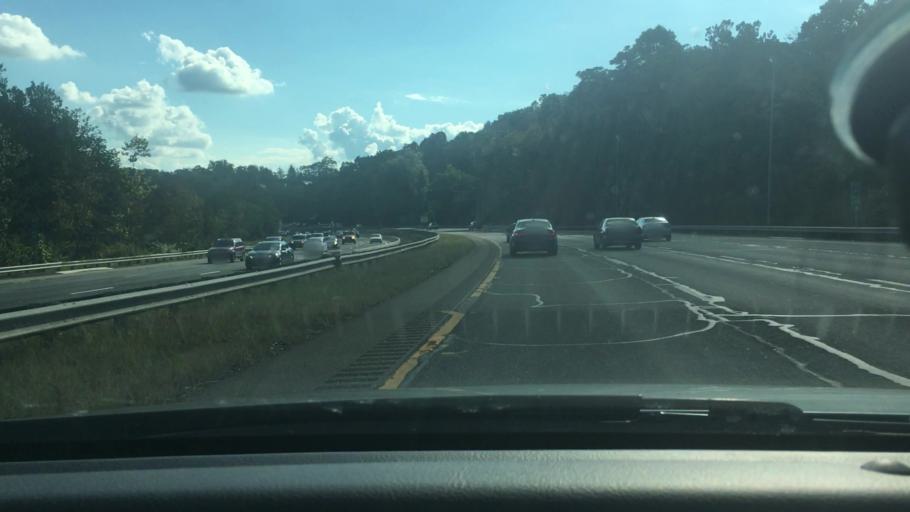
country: US
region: New Jersey
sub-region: Morris County
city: Boonton
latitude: 40.9010
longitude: -74.4124
